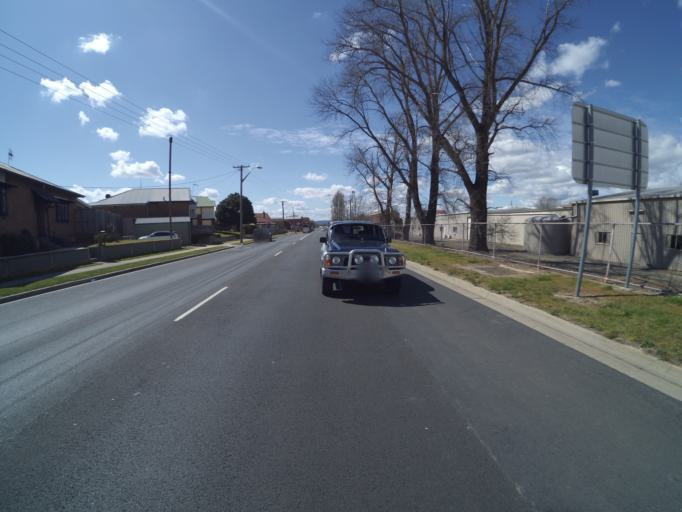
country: AU
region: New South Wales
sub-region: Goulburn Mulwaree
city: Goulburn
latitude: -34.7612
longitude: 149.7159
